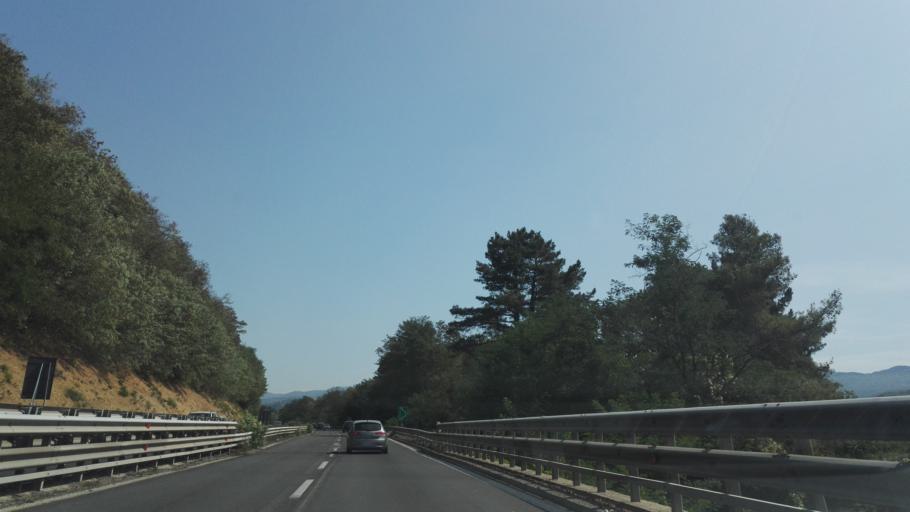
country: IT
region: Calabria
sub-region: Provincia di Cosenza
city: Marzi
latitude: 39.1805
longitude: 16.3009
